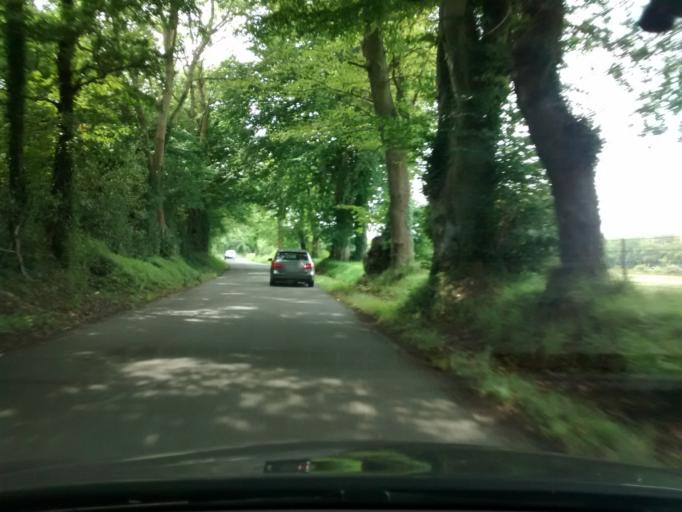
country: FR
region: Lower Normandy
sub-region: Departement du Calvados
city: Deauville
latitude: 49.3356
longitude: 0.0742
